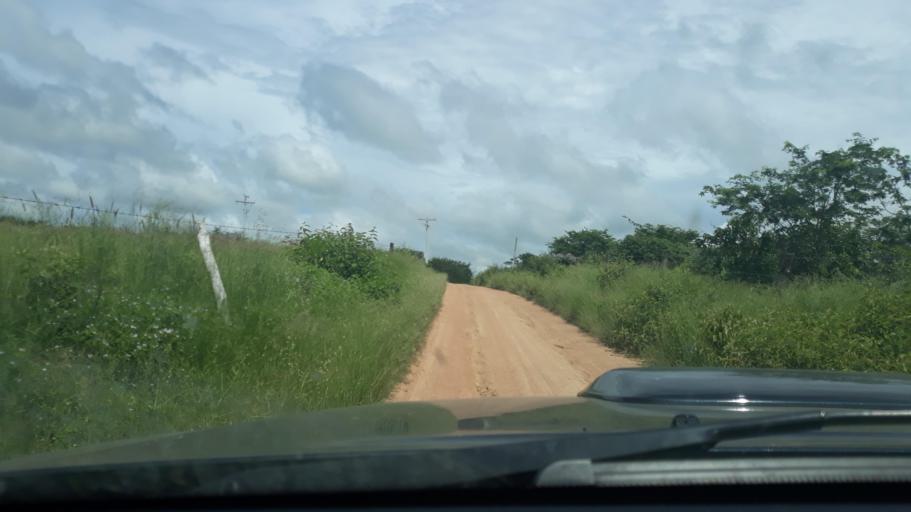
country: BR
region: Bahia
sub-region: Riacho De Santana
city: Riacho de Santana
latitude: -13.8960
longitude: -43.0131
